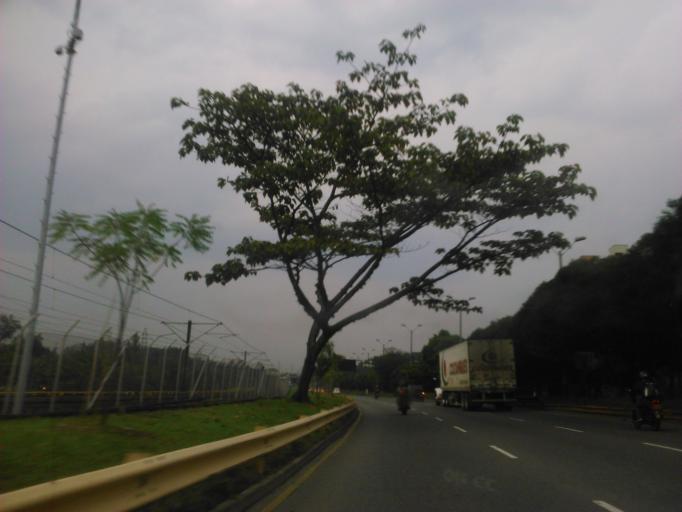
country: CO
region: Antioquia
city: Envigado
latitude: 6.1889
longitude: -75.5830
